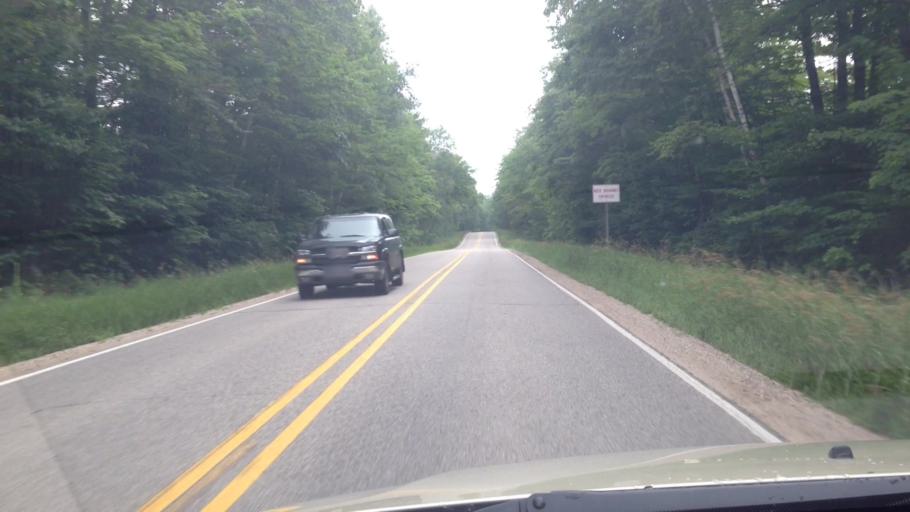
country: US
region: Michigan
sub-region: Mackinac County
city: Saint Ignace
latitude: 46.0407
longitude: -85.1129
